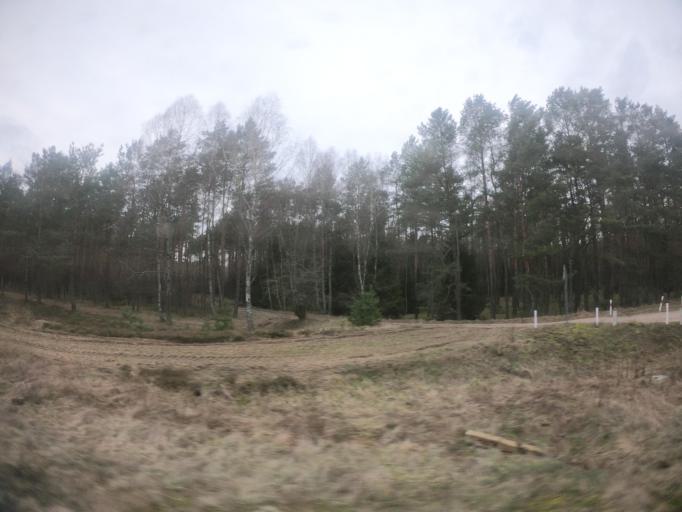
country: PL
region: Pomeranian Voivodeship
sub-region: Powiat czluchowski
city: Czarne
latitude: 53.7481
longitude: 16.8472
